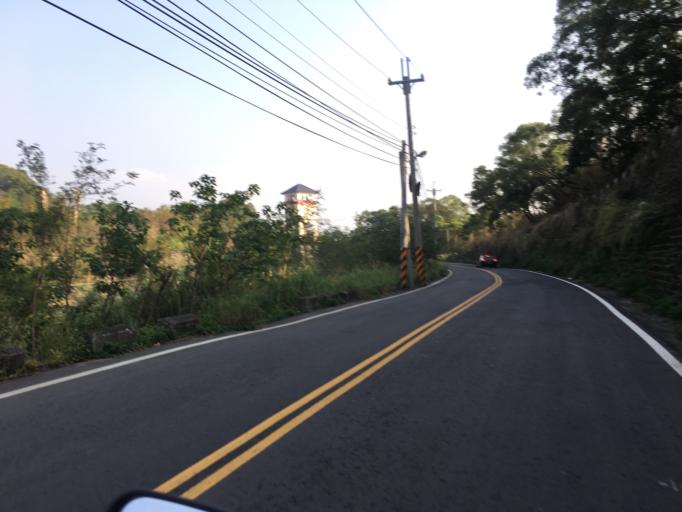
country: TW
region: Taiwan
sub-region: Hsinchu
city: Hsinchu
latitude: 24.7491
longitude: 121.0340
